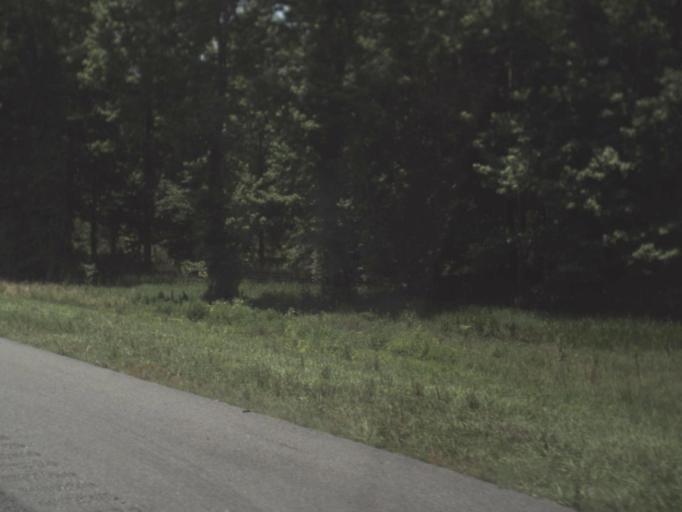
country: US
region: Florida
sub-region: Suwannee County
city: Wellborn
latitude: 30.2700
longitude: -82.7688
